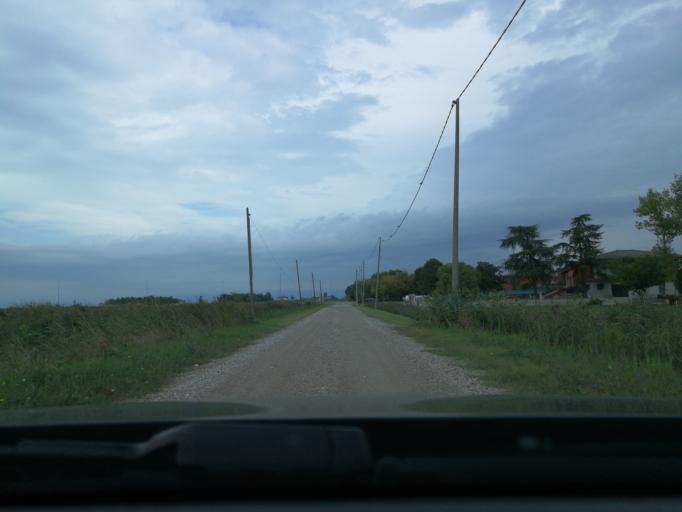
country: IT
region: Friuli Venezia Giulia
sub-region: Provincia di Udine
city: Pertegada
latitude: 45.7214
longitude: 13.0689
